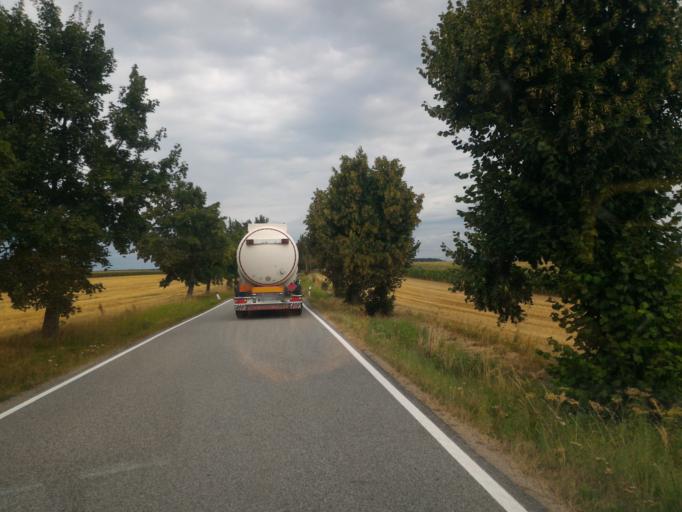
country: CZ
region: Vysocina
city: Zeletava
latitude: 49.1692
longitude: 15.5870
